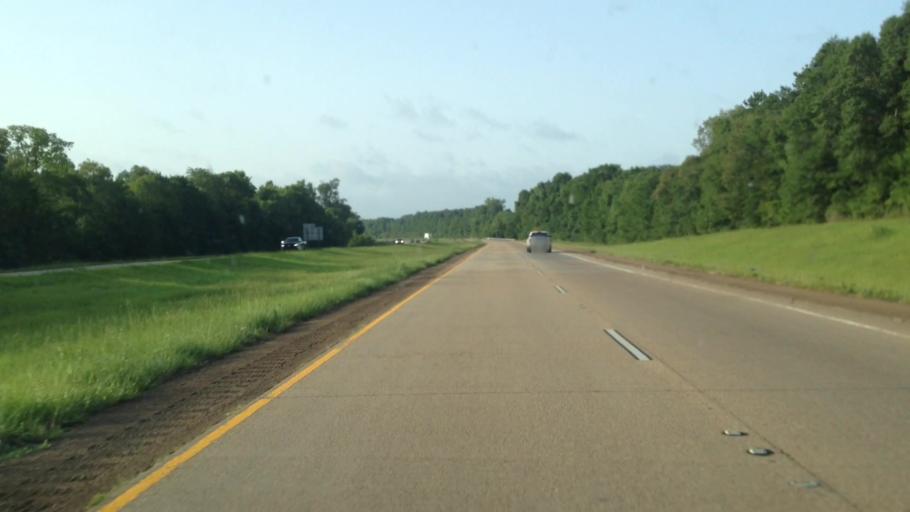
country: US
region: Louisiana
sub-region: Rapides Parish
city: Woodworth
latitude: 31.1472
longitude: -92.4530
